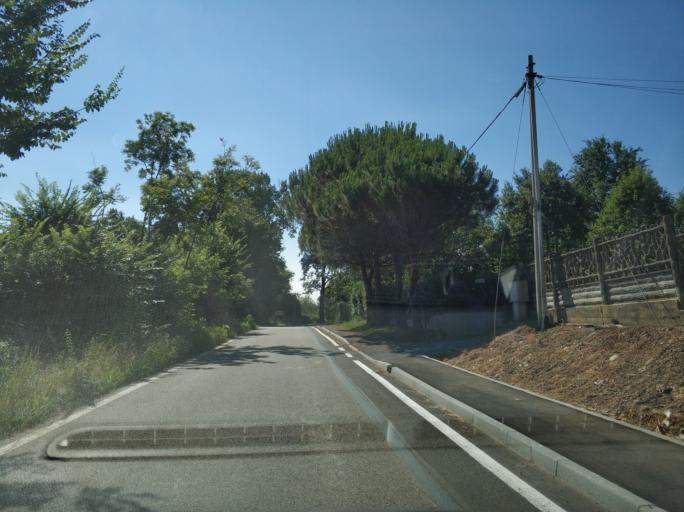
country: IT
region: Piedmont
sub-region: Provincia di Torino
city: Lombardore
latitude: 45.2384
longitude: 7.7251
